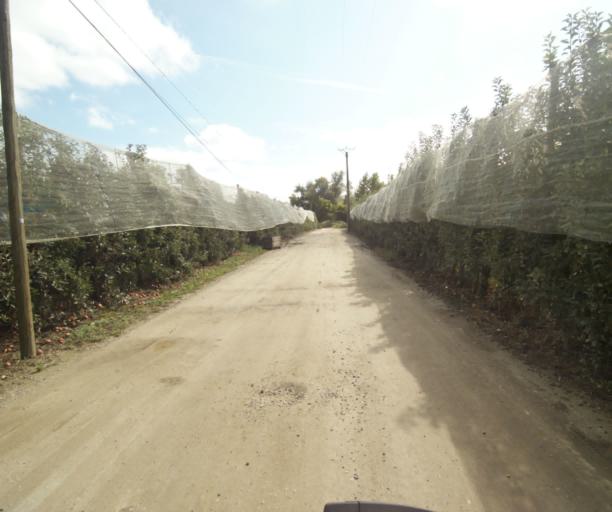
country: FR
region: Midi-Pyrenees
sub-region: Departement du Tarn-et-Garonne
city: Montech
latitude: 43.9521
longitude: 1.1865
